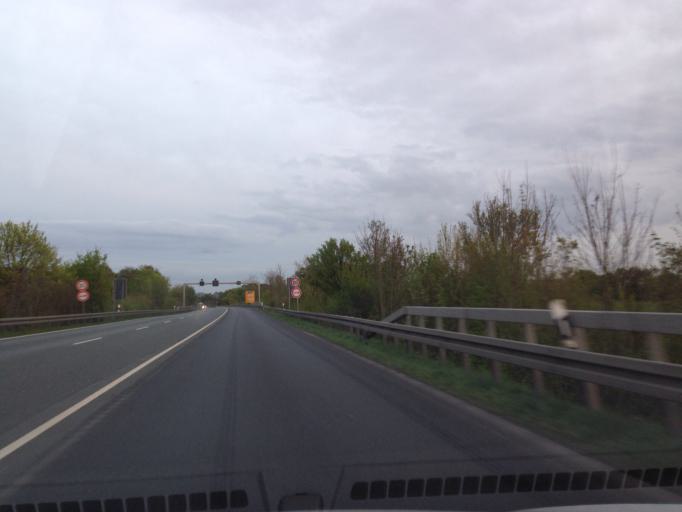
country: DE
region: North Rhine-Westphalia
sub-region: Regierungsbezirk Munster
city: Altenberge
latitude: 52.0521
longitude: 7.4426
